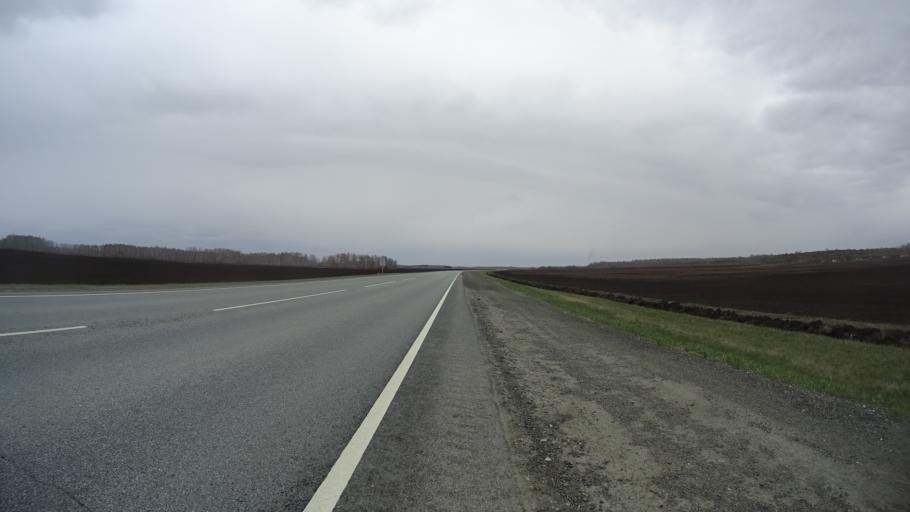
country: RU
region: Chelyabinsk
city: Krasnogorskiy
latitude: 54.5796
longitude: 61.2914
